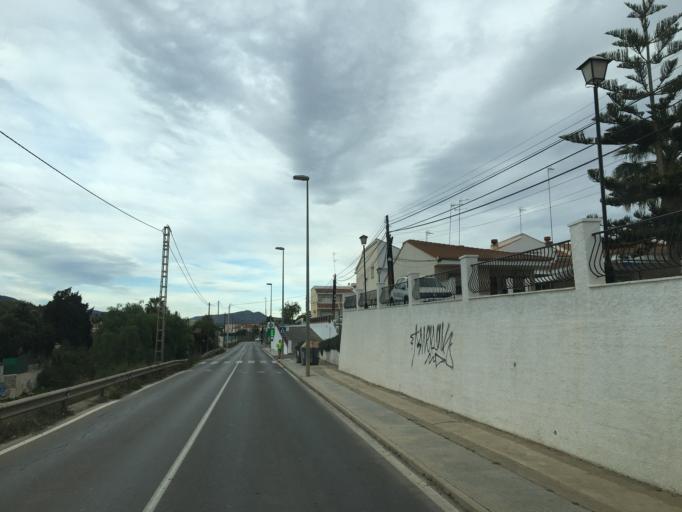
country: ES
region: Murcia
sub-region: Murcia
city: Cartagena
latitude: 37.6114
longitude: -1.0335
